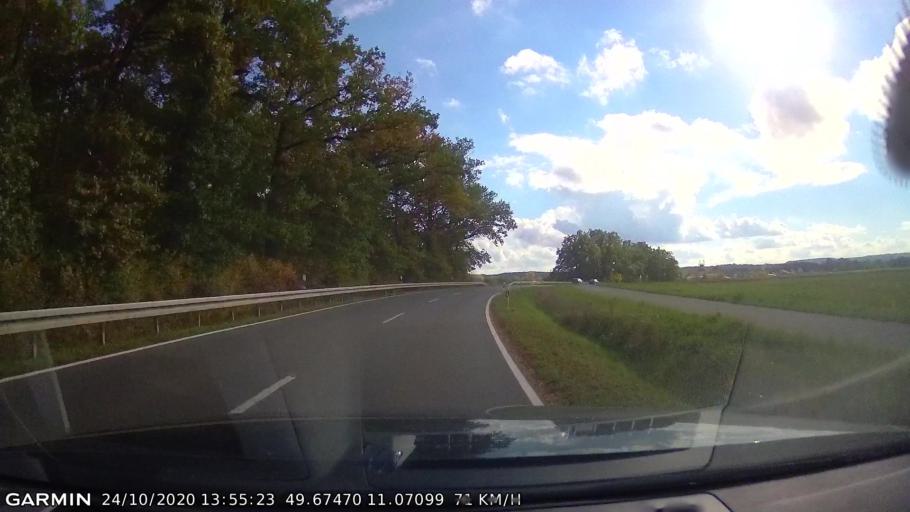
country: DE
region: Bavaria
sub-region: Upper Franconia
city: Poxdorf
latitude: 49.6744
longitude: 11.0708
